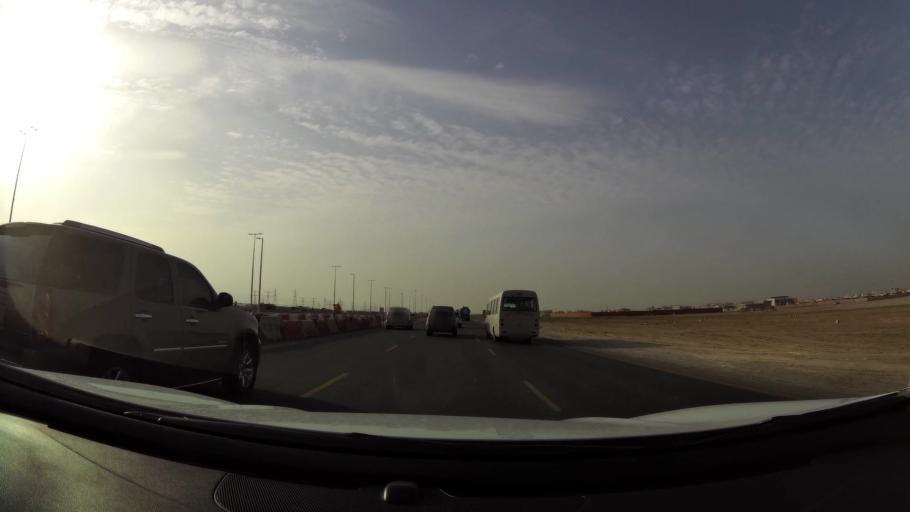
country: AE
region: Abu Dhabi
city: Abu Dhabi
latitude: 24.2977
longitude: 54.5425
